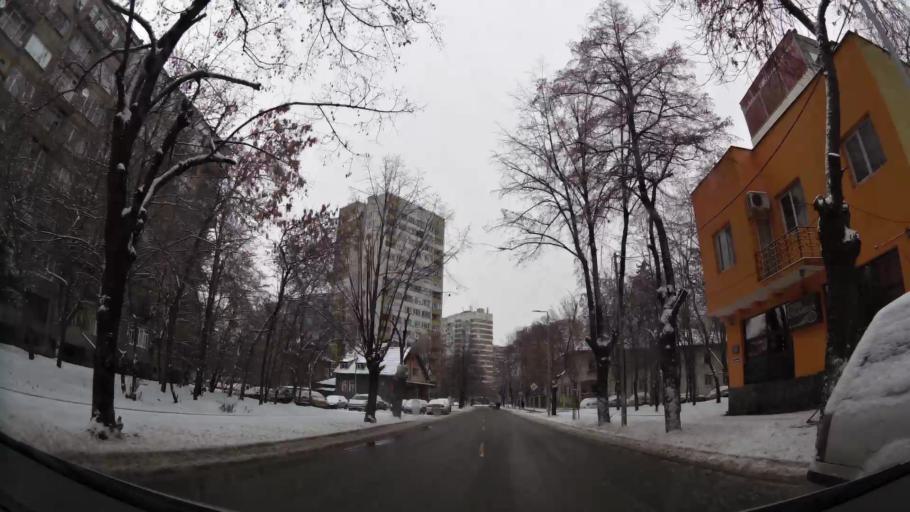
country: BG
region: Sofia-Capital
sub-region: Stolichna Obshtina
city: Sofia
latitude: 42.6957
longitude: 23.3007
